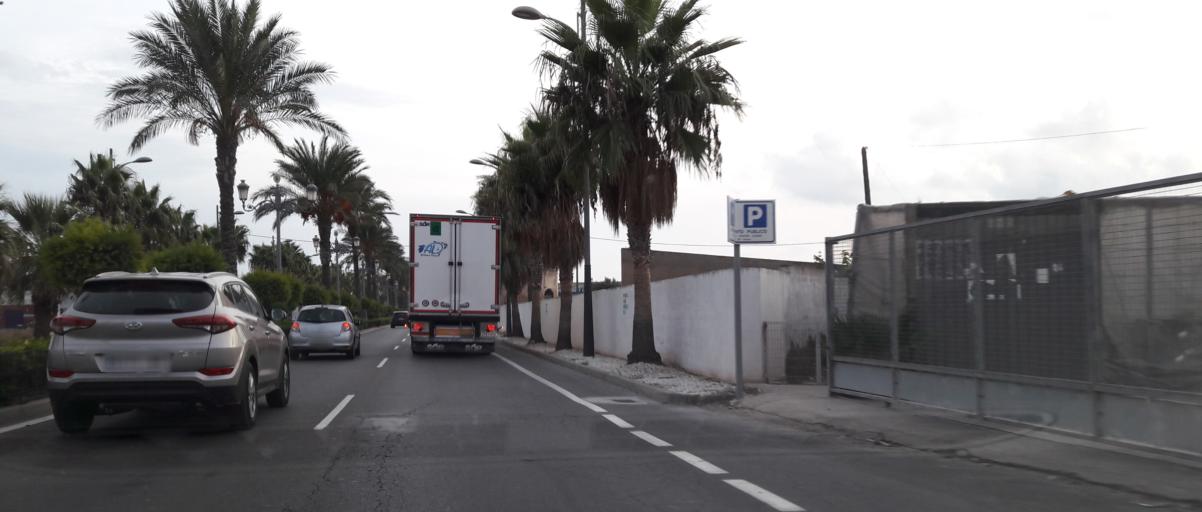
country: ES
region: Andalusia
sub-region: Provincia de Almeria
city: Roquetas de Mar
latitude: 36.7905
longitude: -2.6051
